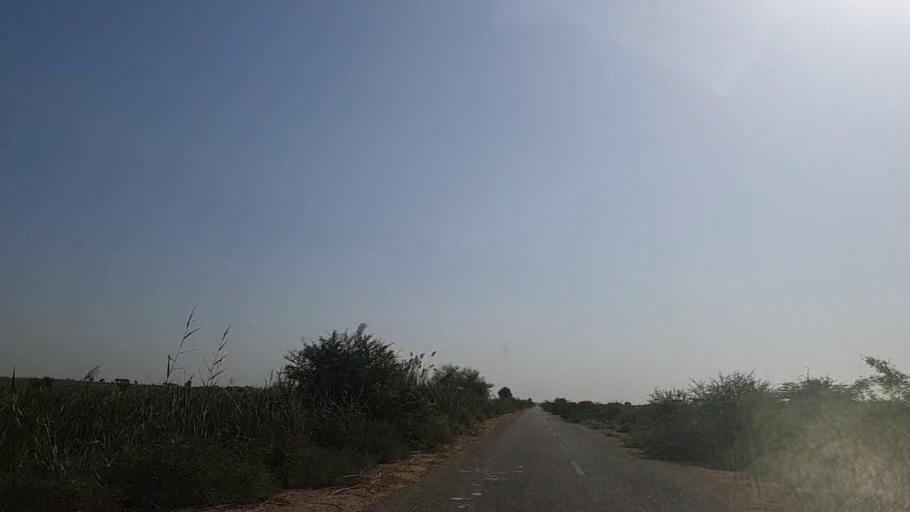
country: PK
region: Sindh
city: Jati
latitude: 24.4429
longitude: 68.2618
